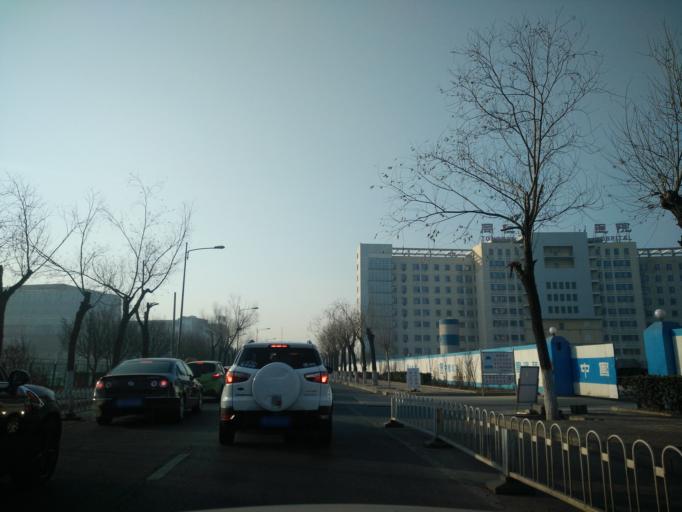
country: CN
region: Beijing
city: Jiugong
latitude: 39.7745
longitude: 116.5159
